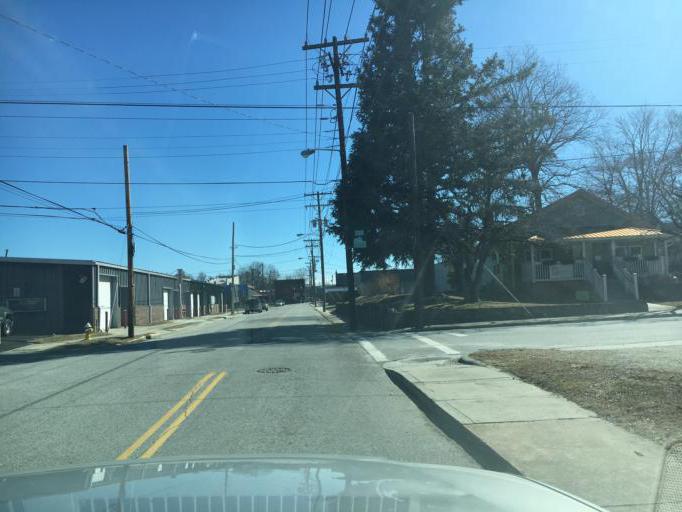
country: US
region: North Carolina
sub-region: Henderson County
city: Hendersonville
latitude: 35.3222
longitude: -82.4594
